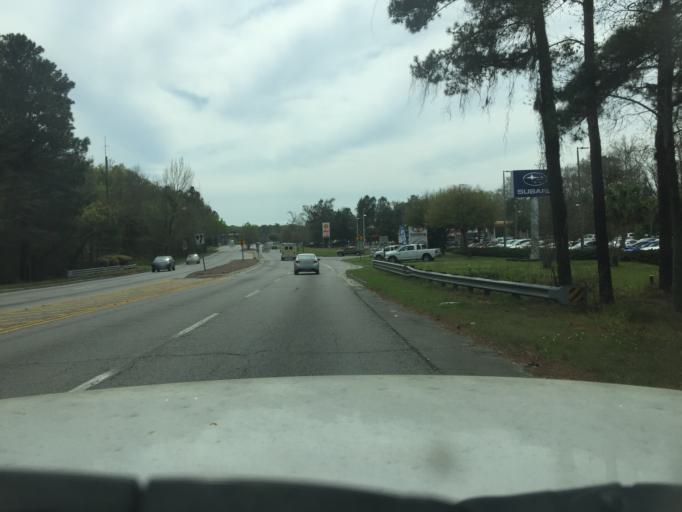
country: US
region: Georgia
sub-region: Chatham County
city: Garden City
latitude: 32.0687
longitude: -81.1609
